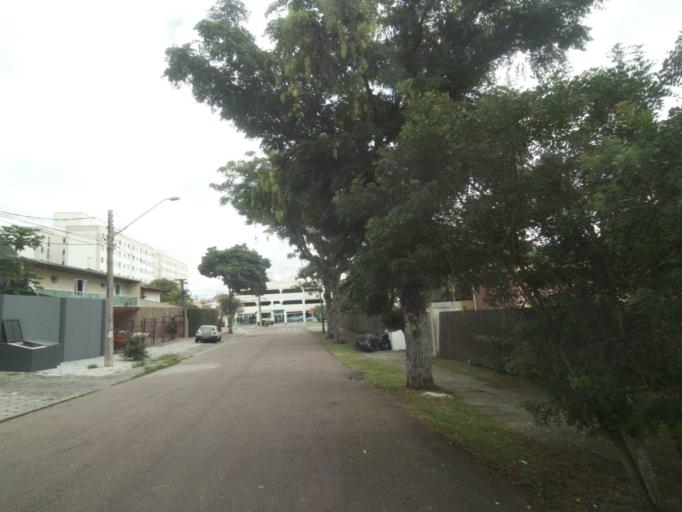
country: BR
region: Parana
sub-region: Curitiba
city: Curitiba
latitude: -25.4805
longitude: -49.2709
